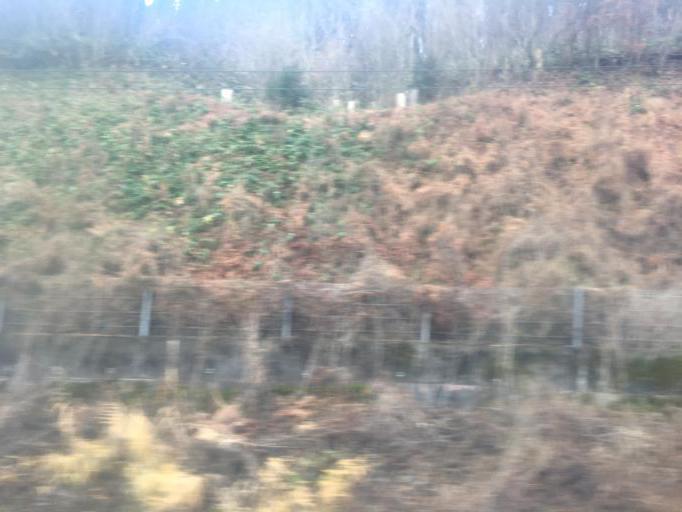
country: JP
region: Akita
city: Takanosu
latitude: 40.2612
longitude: 140.4066
